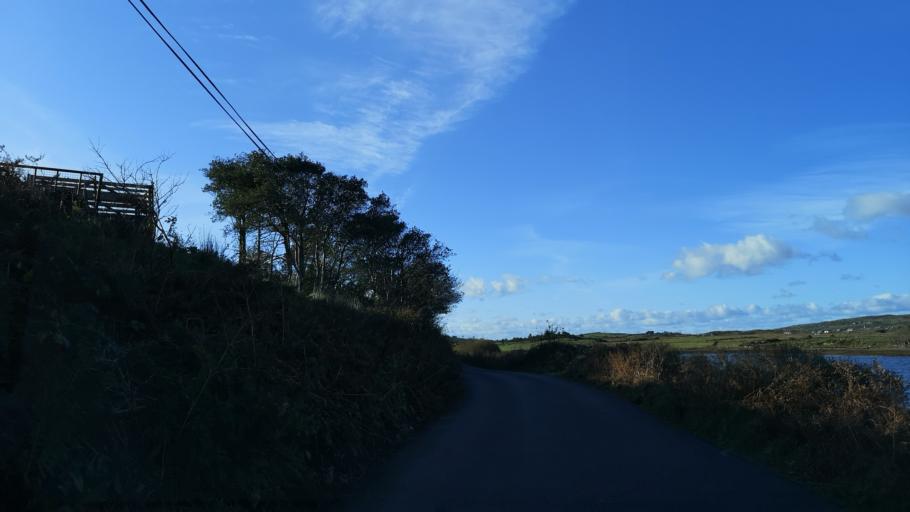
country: IE
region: Connaught
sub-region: County Galway
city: Clifden
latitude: 53.5058
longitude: -10.0744
